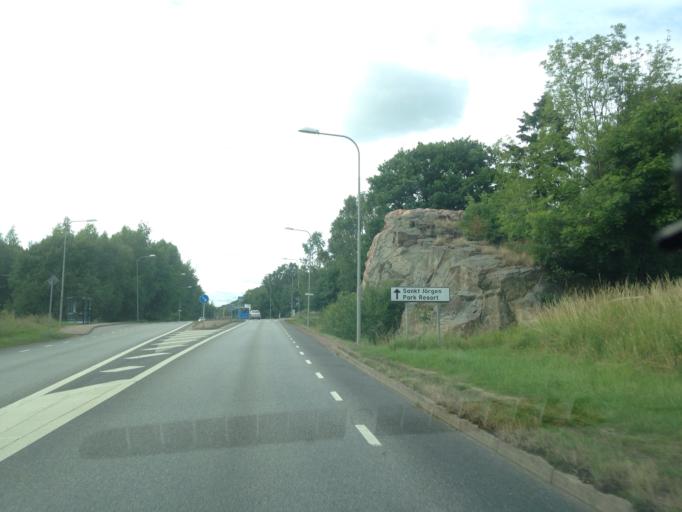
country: SE
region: Vaestra Goetaland
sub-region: Goteborg
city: Goeteborg
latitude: 57.7434
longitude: 11.9529
